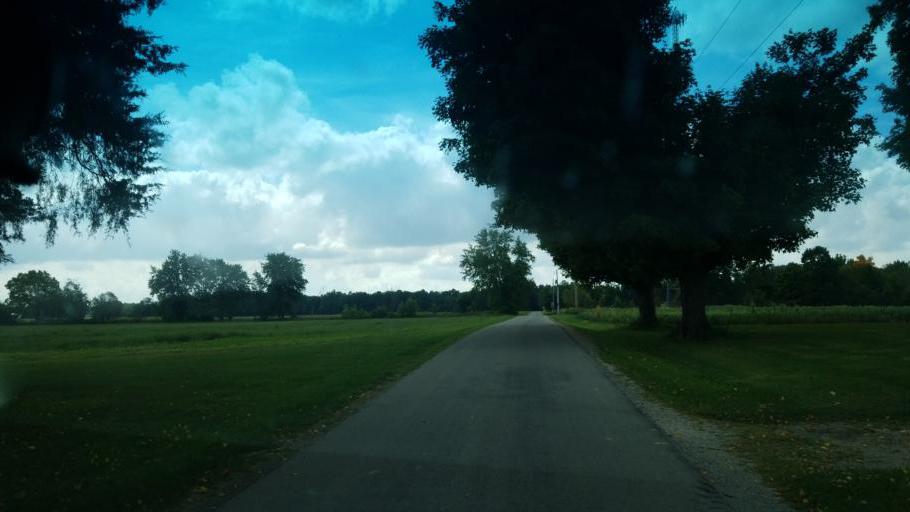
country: US
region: Ohio
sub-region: Seneca County
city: Tiffin
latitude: 40.9591
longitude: -83.1509
